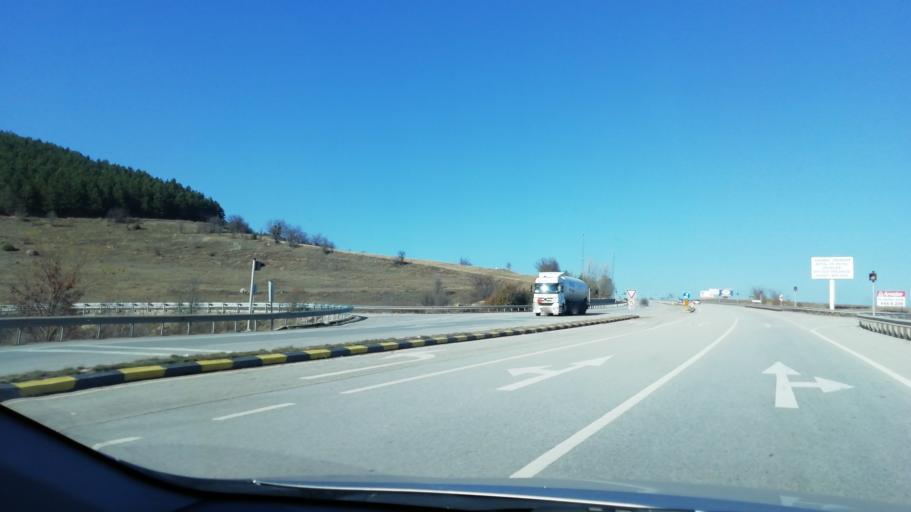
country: TR
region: Karabuk
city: Gozyeri
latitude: 40.8776
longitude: 32.5800
